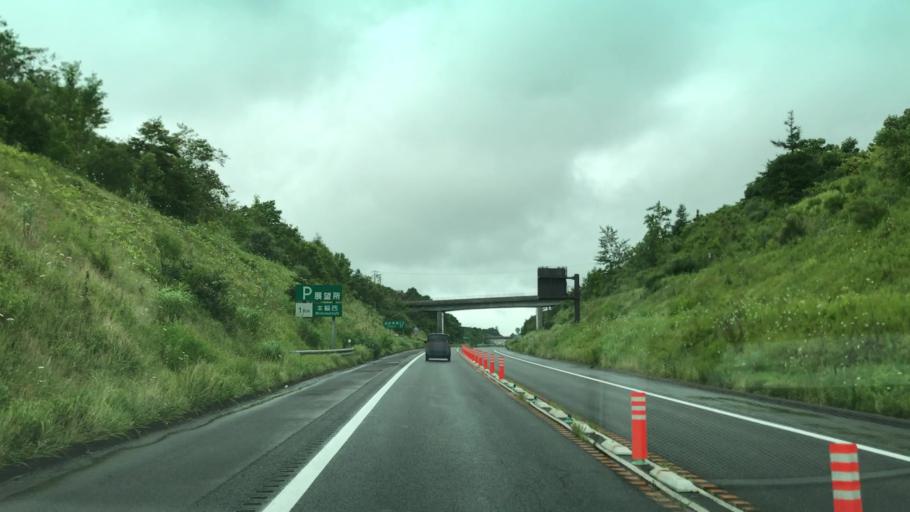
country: JP
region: Hokkaido
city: Muroran
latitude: 42.3833
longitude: 141.0029
